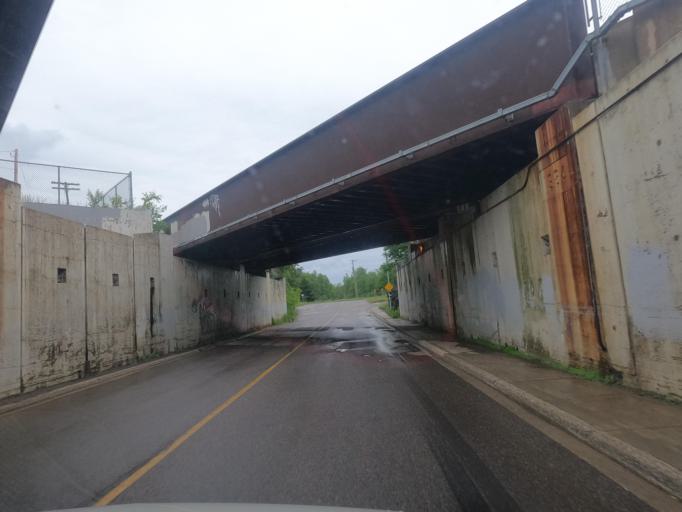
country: CA
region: Ontario
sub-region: Thunder Bay District
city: Thunder Bay
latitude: 48.4544
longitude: -89.1834
